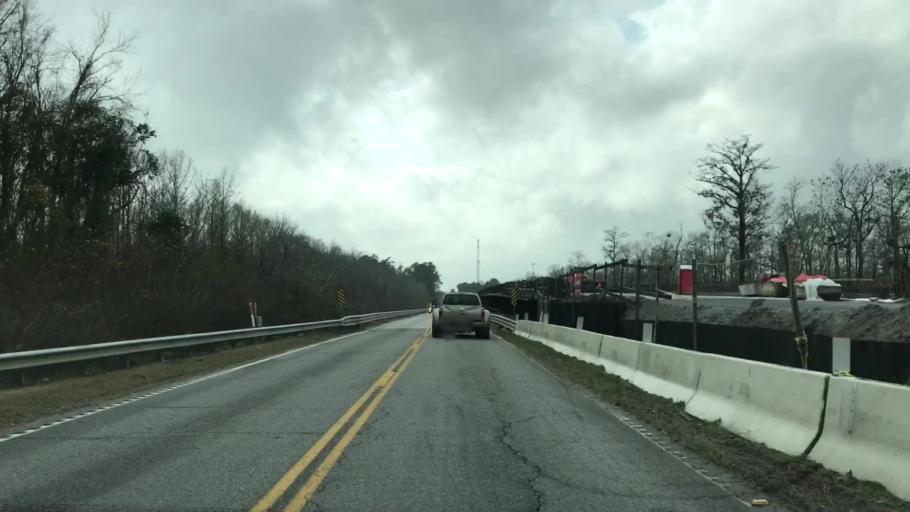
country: US
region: South Carolina
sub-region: Georgetown County
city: Murrells Inlet
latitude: 33.6570
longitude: -79.1594
